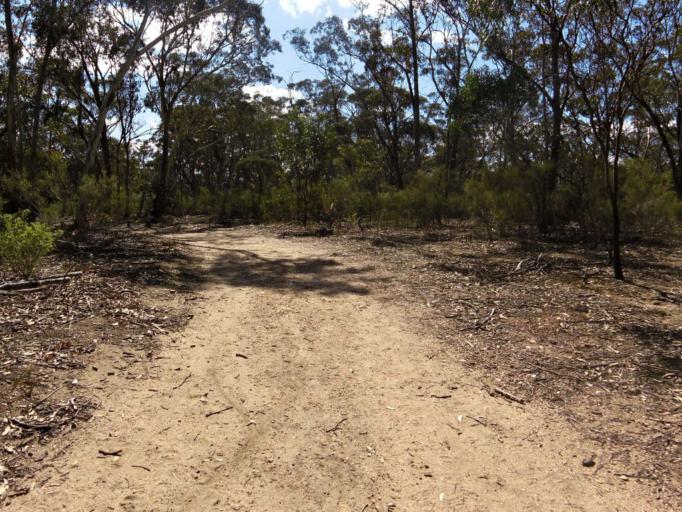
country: AU
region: Victoria
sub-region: Melton
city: Melton West
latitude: -37.6613
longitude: 144.5075
